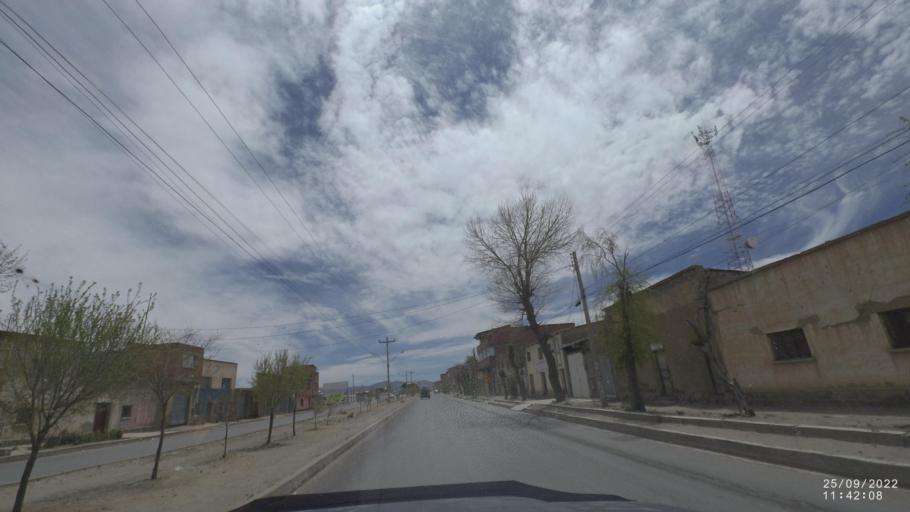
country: BO
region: Oruro
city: Challapata
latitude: -18.8997
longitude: -66.7767
